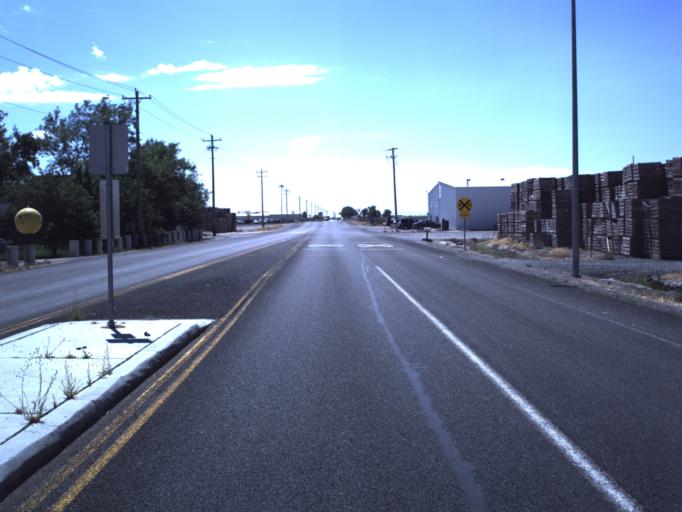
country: US
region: Utah
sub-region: Box Elder County
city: Honeyville
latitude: 41.5656
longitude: -112.1297
